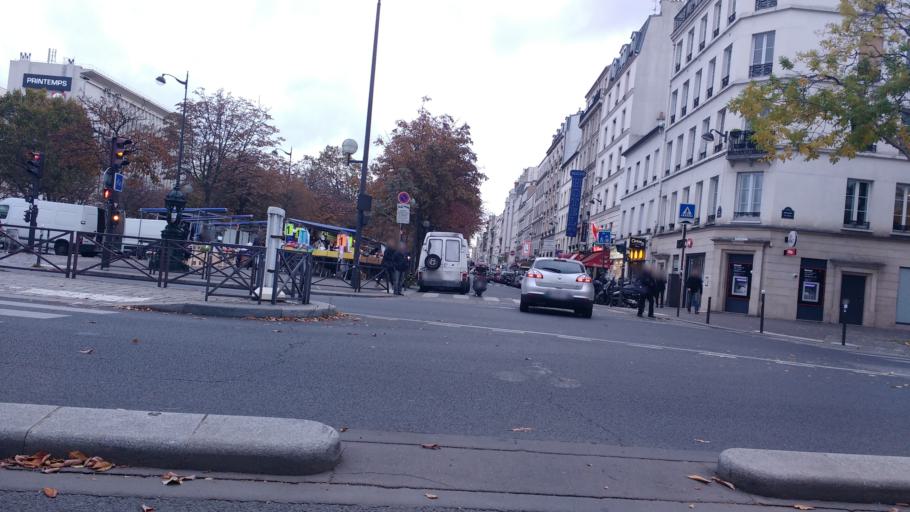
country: FR
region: Ile-de-France
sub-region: Departement du Val-de-Marne
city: Saint-Mande
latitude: 48.8478
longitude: 2.3990
